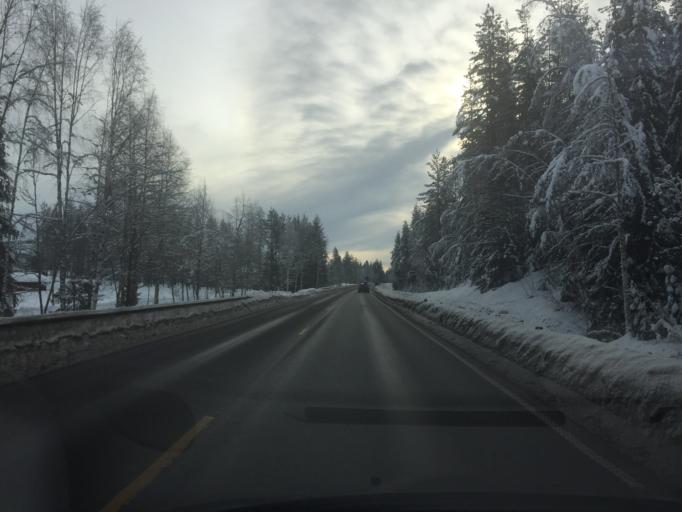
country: NO
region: Hedmark
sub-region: Trysil
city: Innbygda
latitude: 61.2897
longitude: 12.2762
